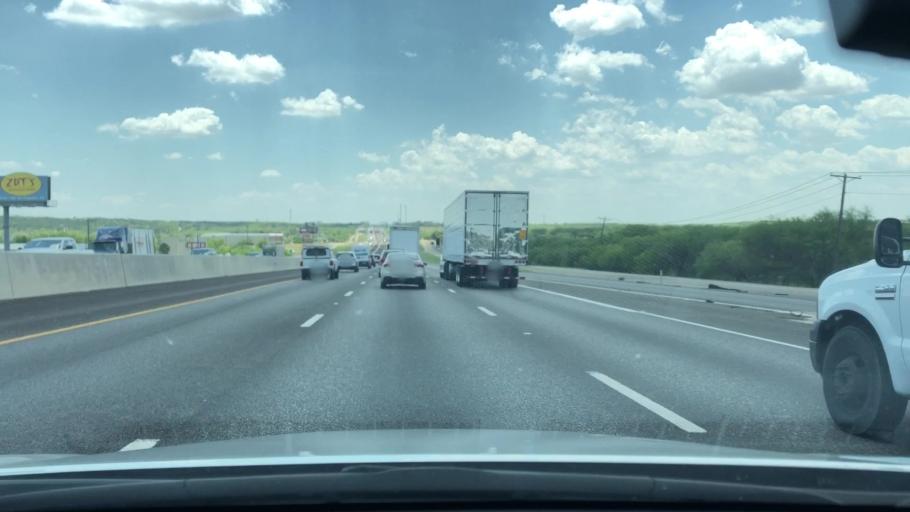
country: US
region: Texas
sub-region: Guadalupe County
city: Lake Dunlap
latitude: 29.7753
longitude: -98.0381
